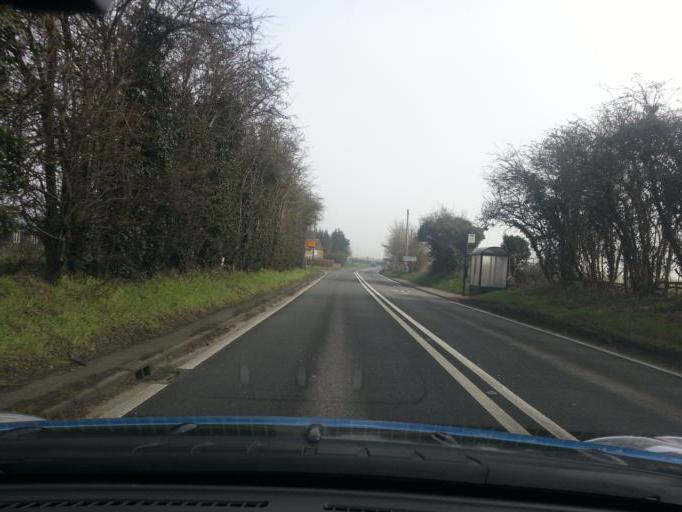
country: GB
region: England
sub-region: Oxfordshire
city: Faringdon
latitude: 51.6692
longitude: -1.5472
